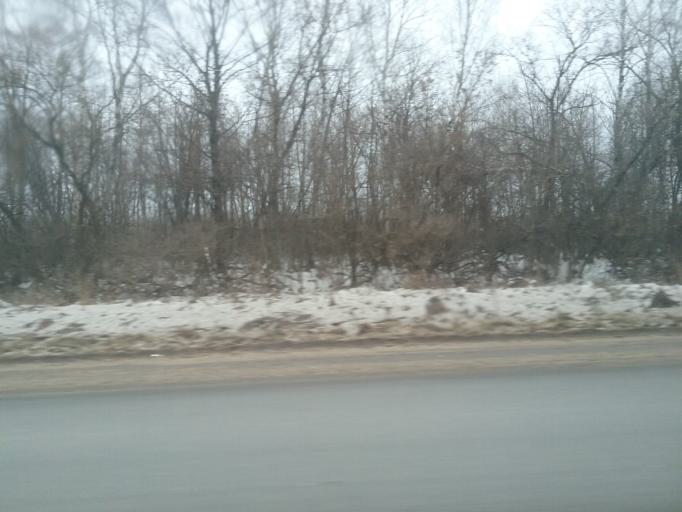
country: RU
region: Tula
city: Bolokhovo
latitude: 54.1008
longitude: 37.7652
